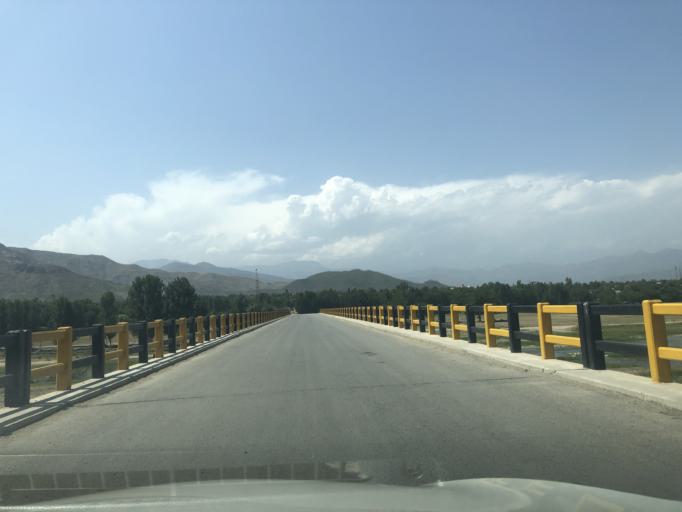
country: PK
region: Khyber Pakhtunkhwa
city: Timurgara
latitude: 34.7925
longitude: 71.6629
